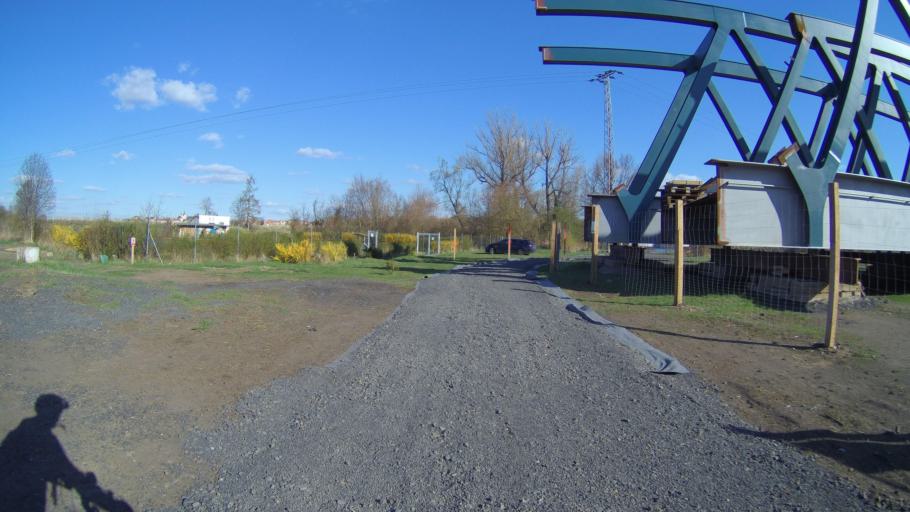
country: CZ
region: Ustecky
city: Zatec
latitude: 50.3314
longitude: 13.5193
